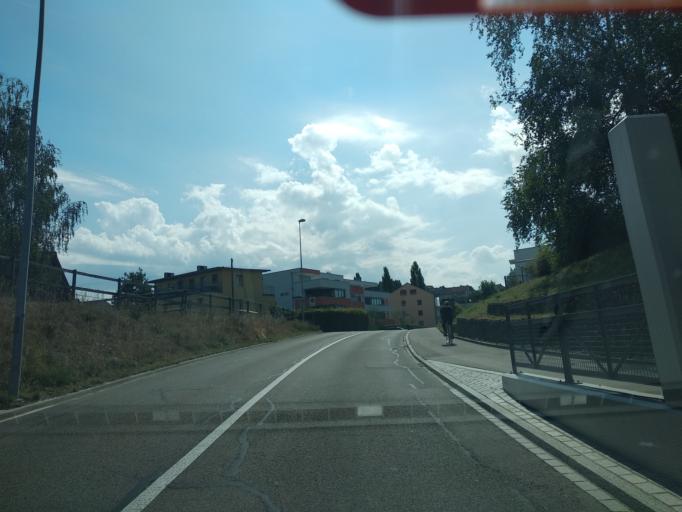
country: CH
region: Thurgau
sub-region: Frauenfeld District
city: Frauenfeld
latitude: 47.5634
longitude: 8.9047
